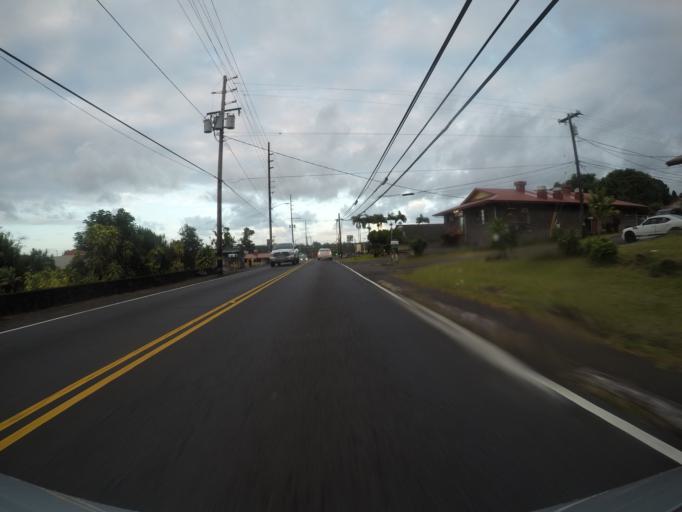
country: US
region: Hawaii
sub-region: Hawaii County
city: Hilo
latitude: 19.6846
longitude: -155.0703
